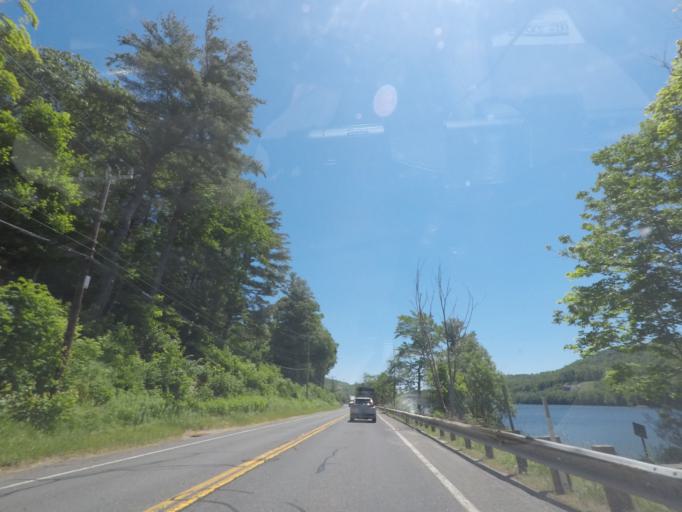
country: US
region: Massachusetts
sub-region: Berkshire County
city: Becket
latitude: 42.2893
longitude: -73.1537
